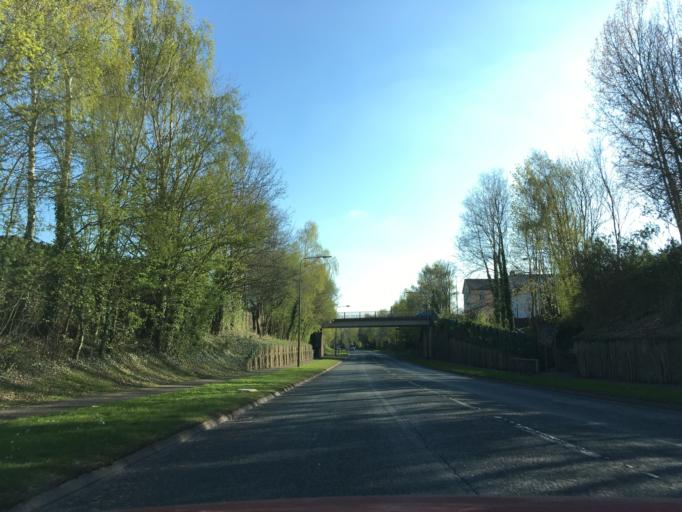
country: GB
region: Wales
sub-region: Torfaen County Borough
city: Cwmbran
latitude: 51.6618
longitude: -3.0236
